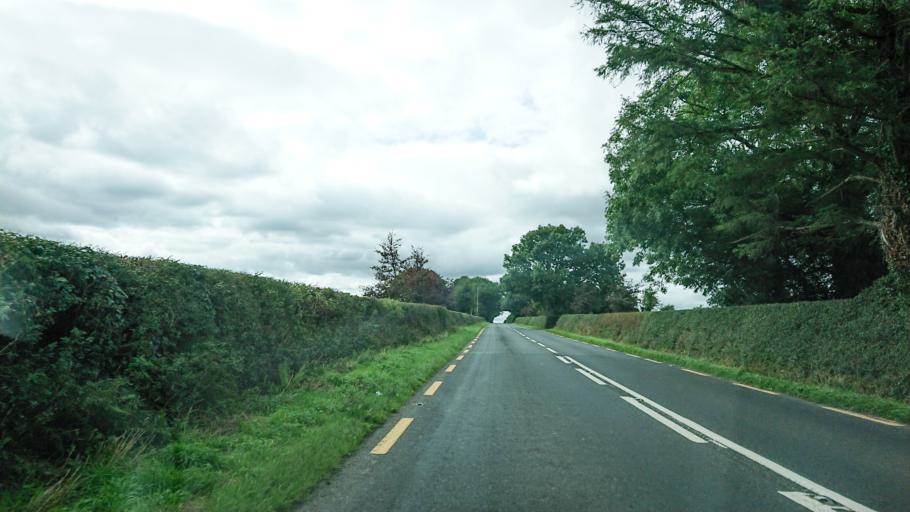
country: IE
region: Munster
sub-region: Waterford
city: Dungarvan
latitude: 52.1102
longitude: -7.6214
